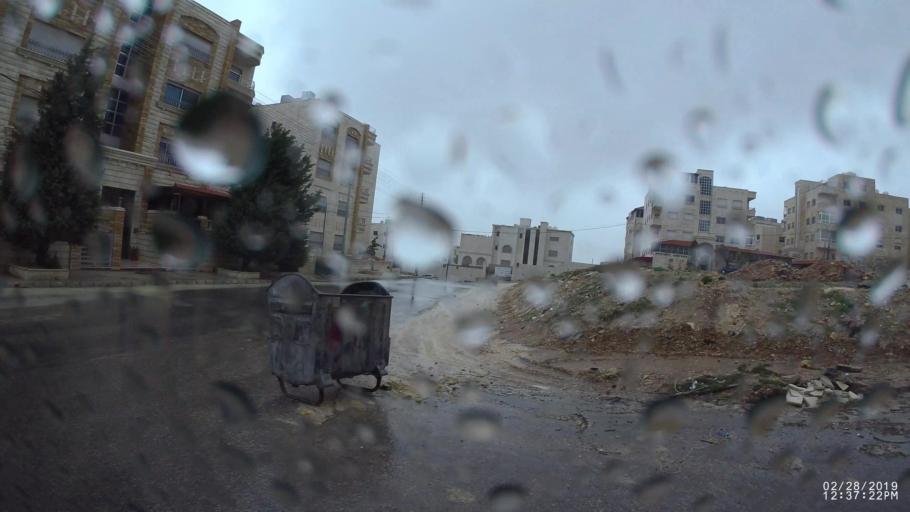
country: JO
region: Amman
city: Al Jubayhah
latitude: 32.0273
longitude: 35.8853
